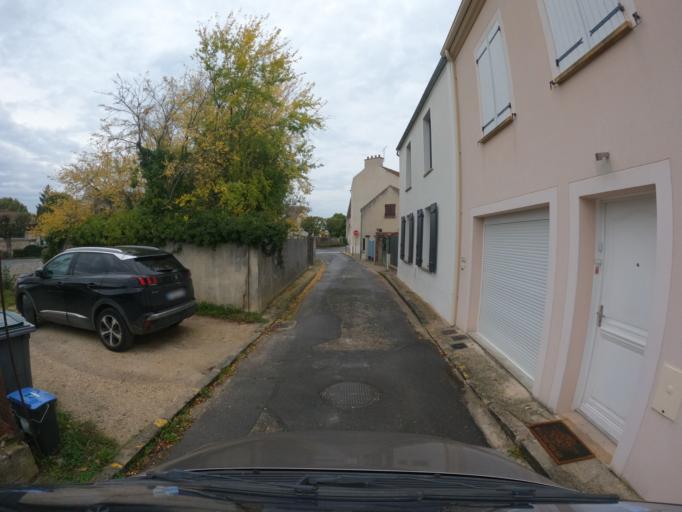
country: FR
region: Ile-de-France
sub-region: Departement de Seine-et-Marne
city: Villeneuve-le-Comte
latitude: 48.8121
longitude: 2.8302
